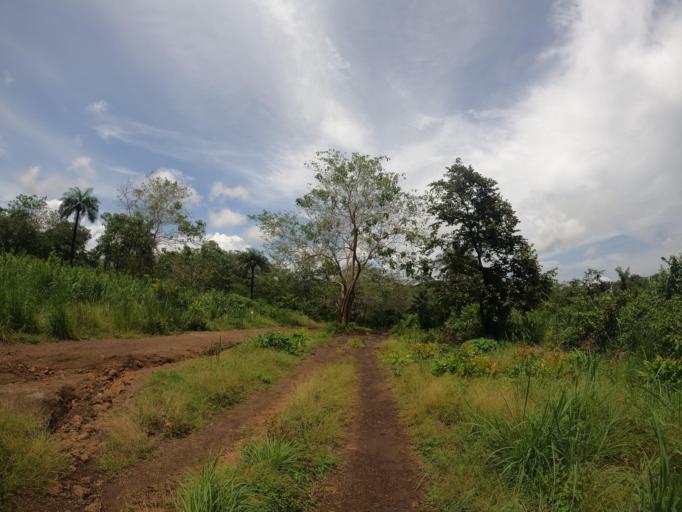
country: SL
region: Northern Province
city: Binkolo
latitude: 9.1573
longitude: -12.2052
